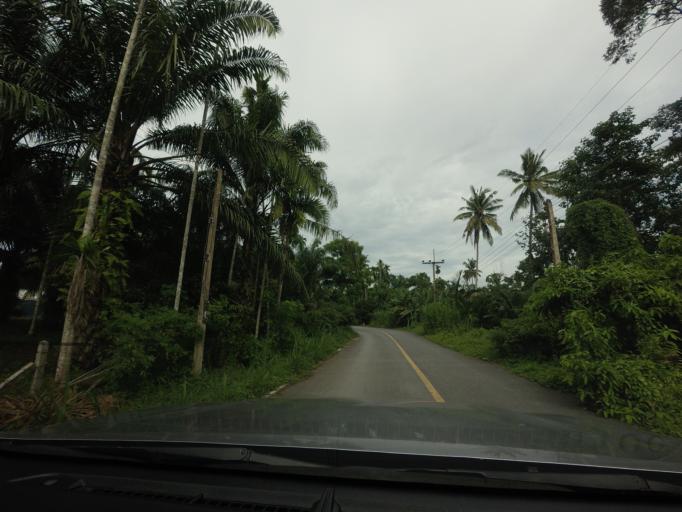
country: TH
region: Nakhon Si Thammarat
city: Phra Phrom
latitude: 8.2853
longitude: 99.9174
